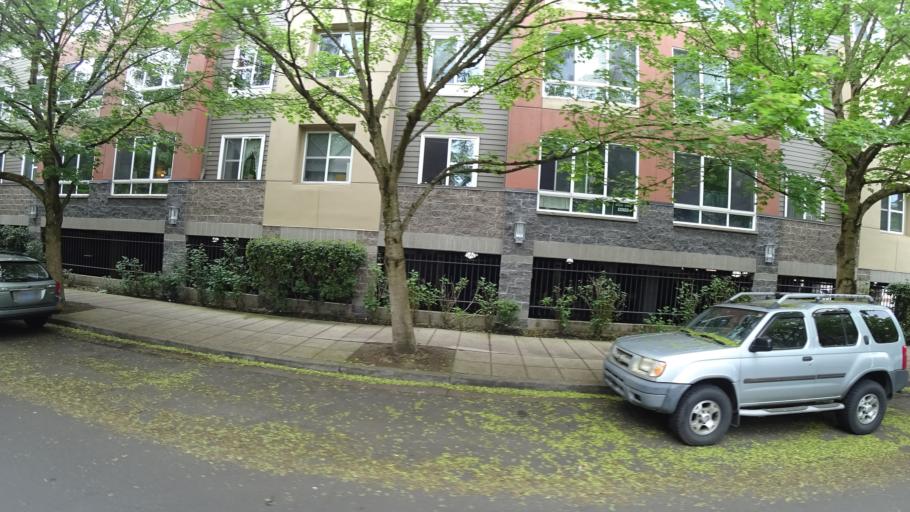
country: US
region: Oregon
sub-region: Multnomah County
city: Portland
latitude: 45.5172
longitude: -122.6303
